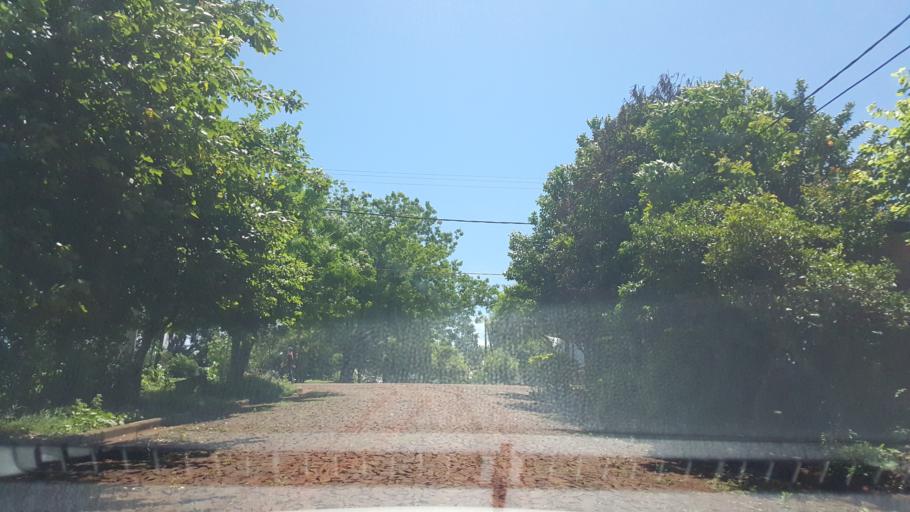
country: AR
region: Misiones
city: Capiovi
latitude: -26.9352
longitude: -55.0615
